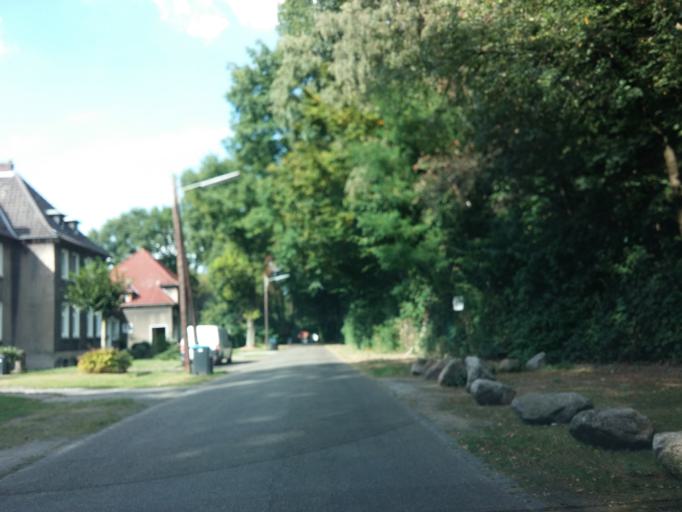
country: DE
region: North Rhine-Westphalia
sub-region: Regierungsbezirk Munster
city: Gladbeck
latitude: 51.5962
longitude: 6.9998
